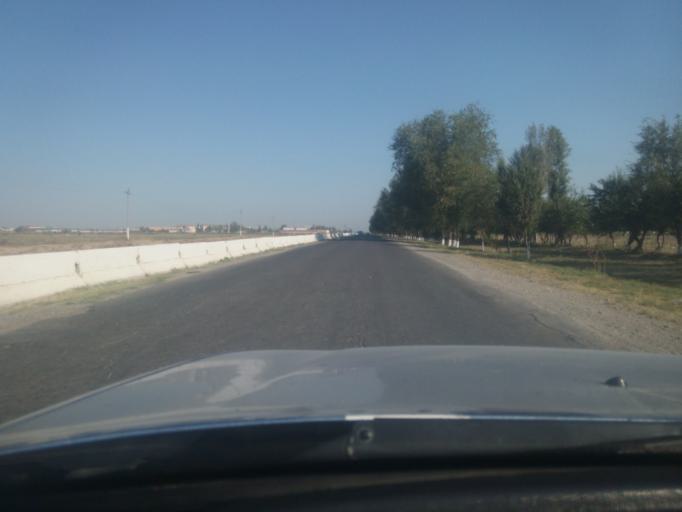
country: UZ
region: Sirdaryo
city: Guliston
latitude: 40.5073
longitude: 68.7964
